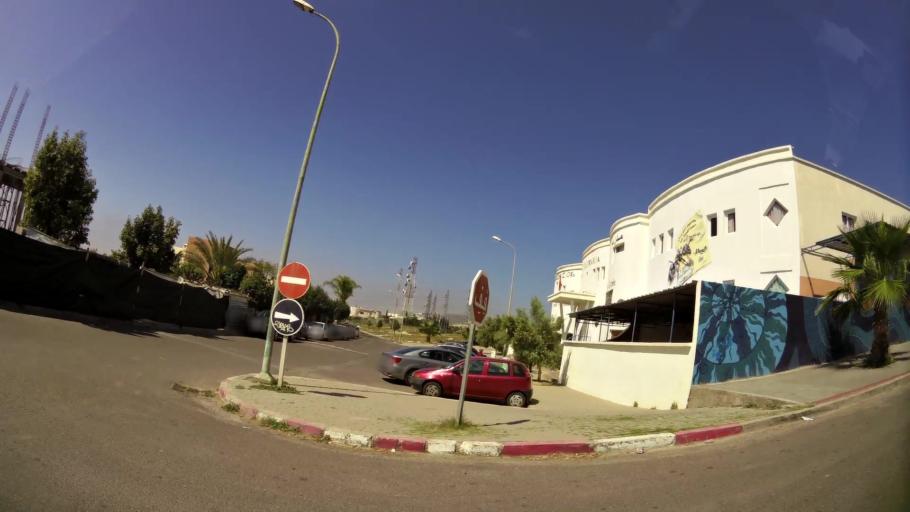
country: MA
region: Souss-Massa-Draa
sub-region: Agadir-Ida-ou-Tnan
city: Agadir
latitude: 30.4415
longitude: -9.5940
